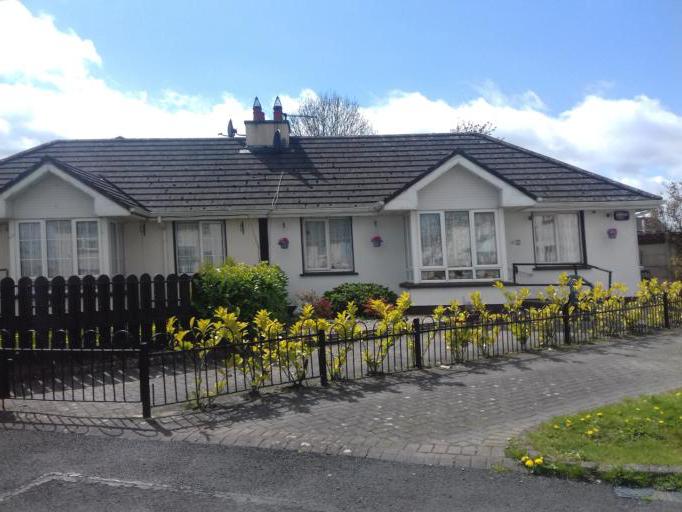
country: IE
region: Leinster
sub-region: Laois
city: Portlaoise
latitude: 53.0405
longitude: -7.3070
